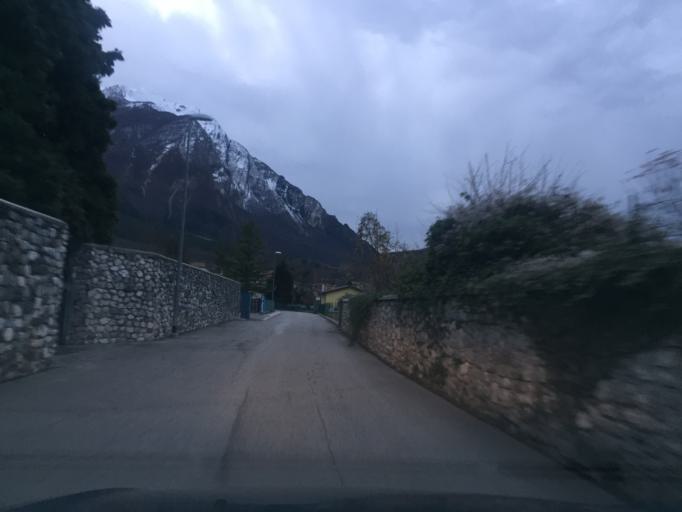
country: IT
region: Friuli Venezia Giulia
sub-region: Provincia di Udine
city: Venzone
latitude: 46.3271
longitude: 13.1361
